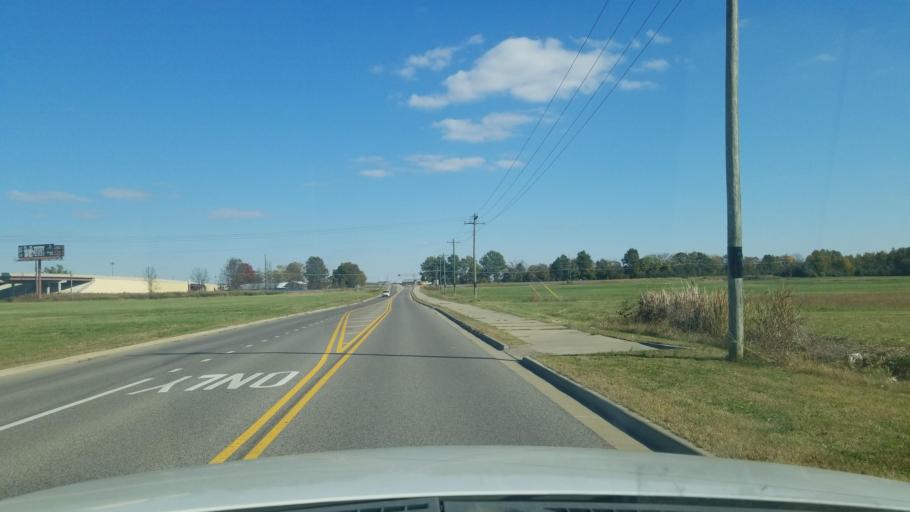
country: US
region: Illinois
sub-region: Williamson County
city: Marion
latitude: 37.7434
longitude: -88.9836
